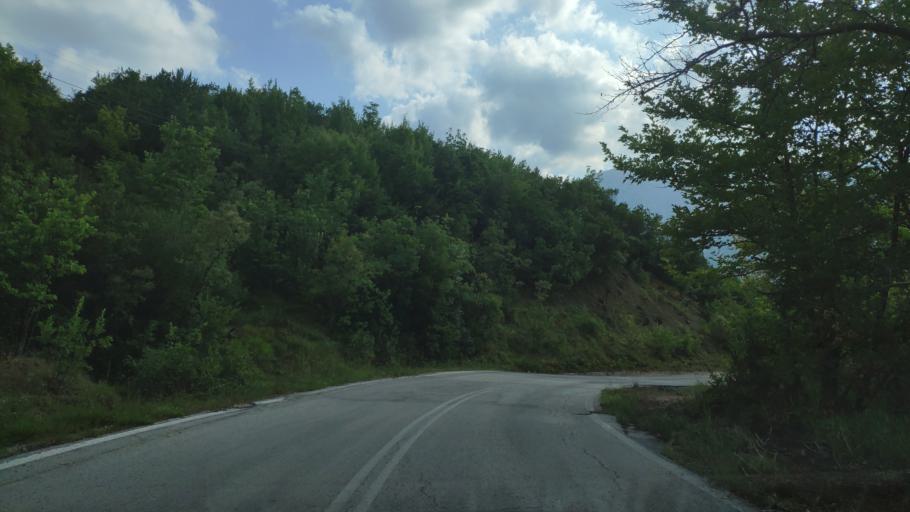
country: GR
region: Epirus
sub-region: Nomos Artas
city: Agios Dimitrios
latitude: 39.4579
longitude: 21.0563
